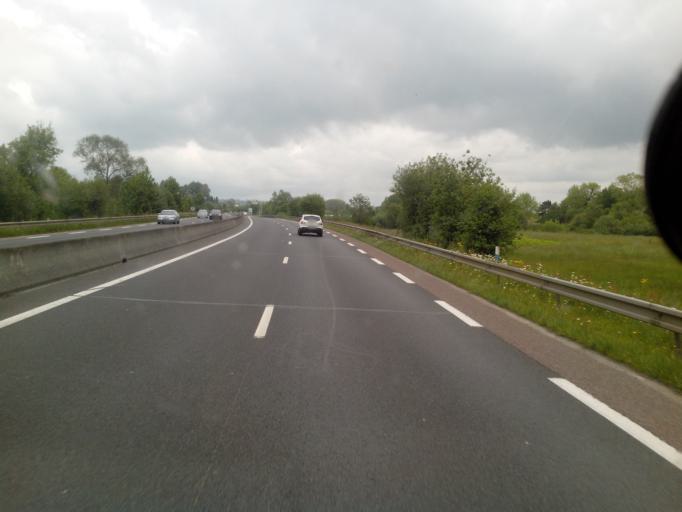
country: FR
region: Lower Normandy
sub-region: Departement de la Manche
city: Avranches
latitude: 48.6954
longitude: -1.3518
